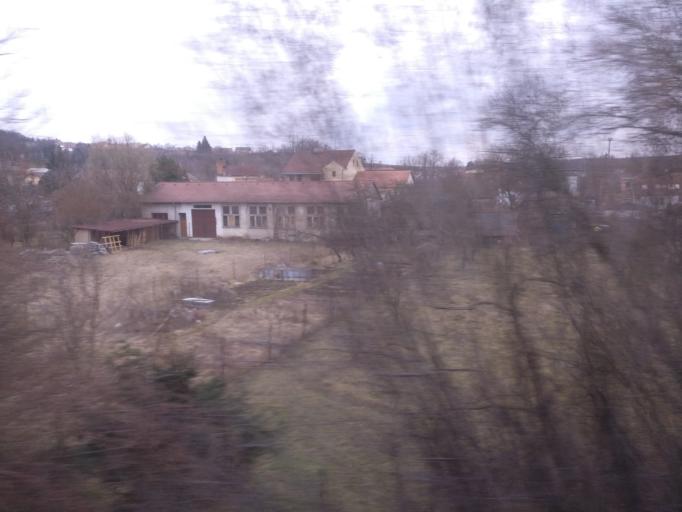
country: CZ
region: South Moravian
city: Zastavka
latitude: 49.1854
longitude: 16.3650
